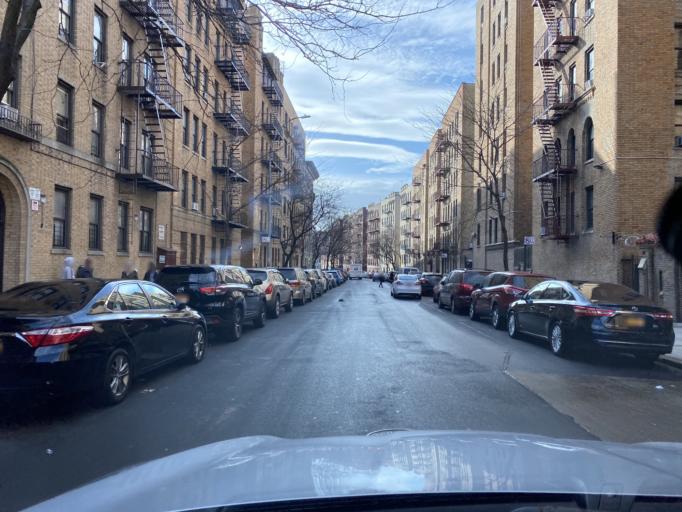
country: US
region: New York
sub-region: Bronx
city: The Bronx
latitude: 40.8672
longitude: -73.8921
